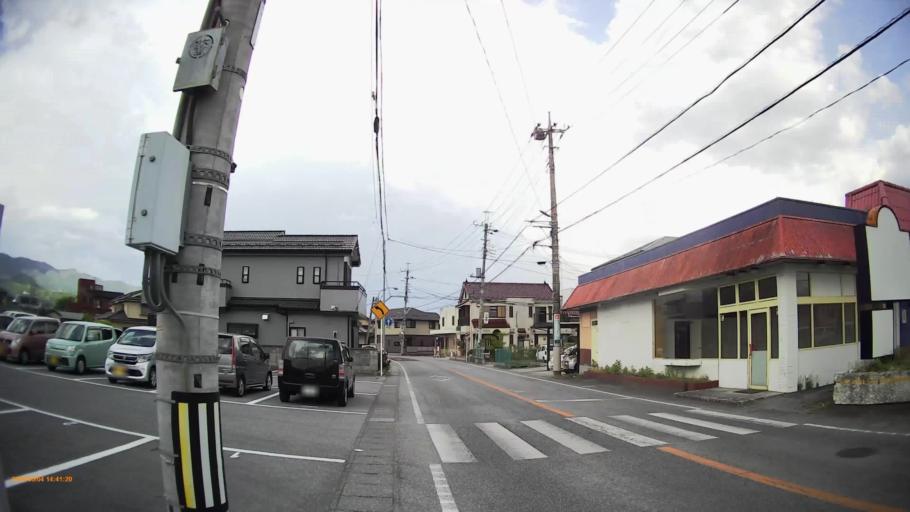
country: JP
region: Yamanashi
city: Kofu-shi
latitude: 35.6585
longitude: 138.5539
